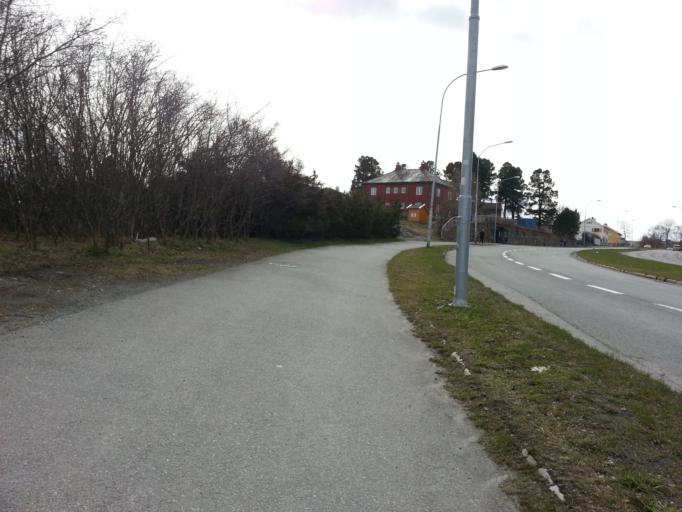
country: NO
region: Sor-Trondelag
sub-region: Trondheim
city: Trondheim
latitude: 63.4189
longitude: 10.3731
